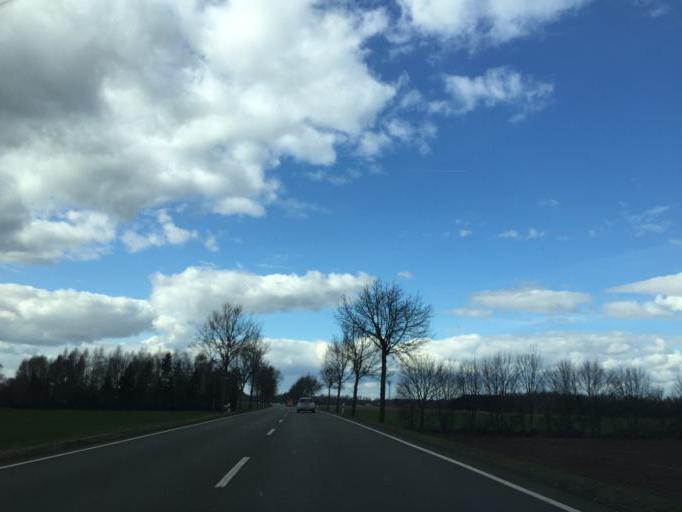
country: DE
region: Lower Saxony
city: Broeckel
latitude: 52.5047
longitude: 10.2305
